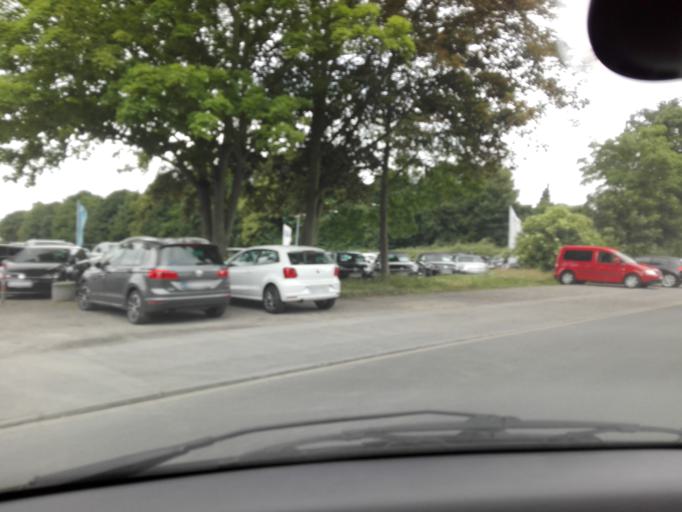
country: DE
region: North Rhine-Westphalia
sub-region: Regierungsbezirk Arnsberg
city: Unna
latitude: 51.5296
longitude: 7.6788
